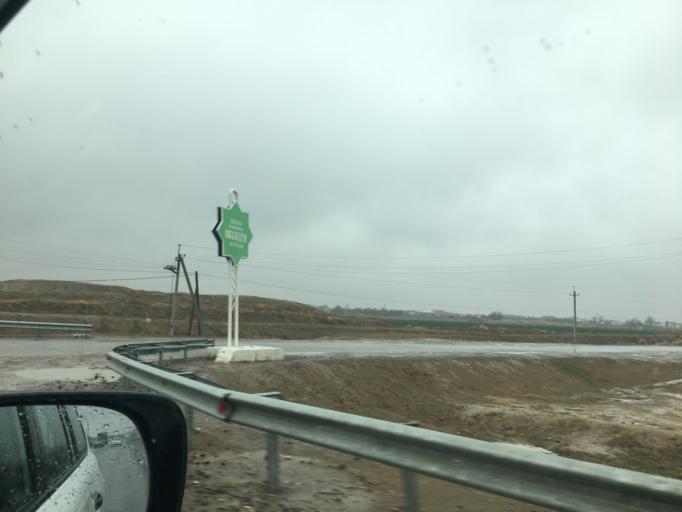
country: TM
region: Mary
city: Yoloeten
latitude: 37.2917
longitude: 62.3398
